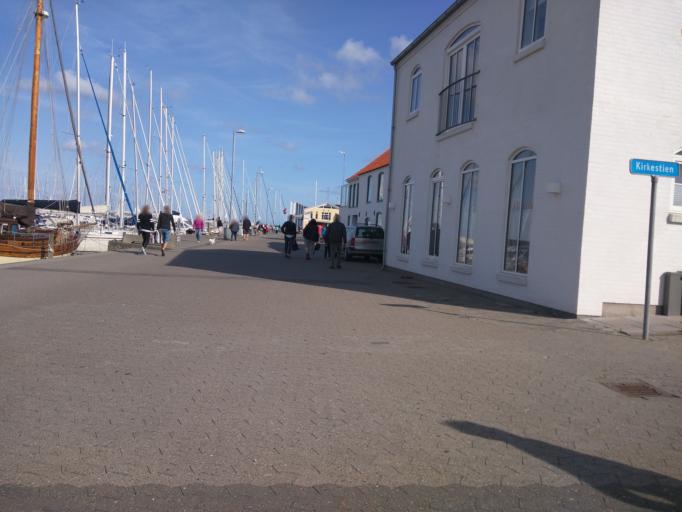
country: DK
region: North Denmark
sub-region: Frederikshavn Kommune
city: Saeby
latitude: 57.3337
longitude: 10.5296
